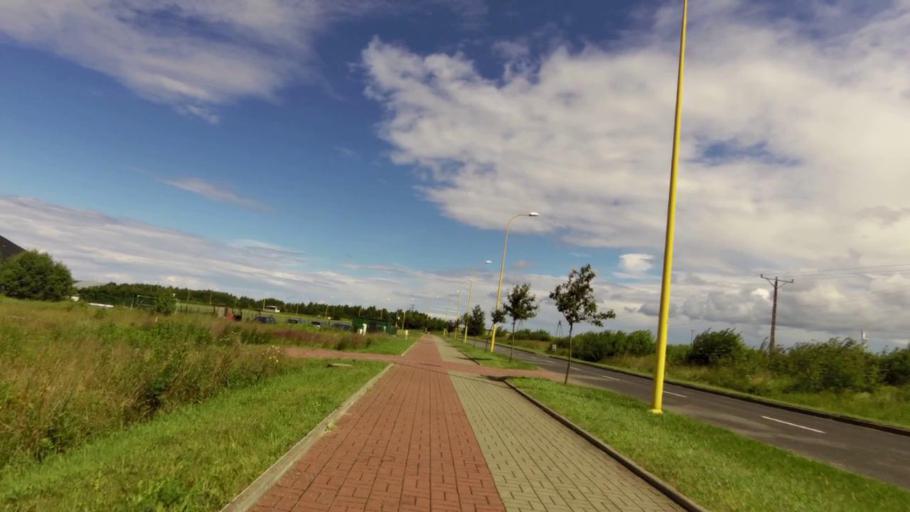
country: PL
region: West Pomeranian Voivodeship
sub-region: Powiat slawienski
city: Darlowo
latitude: 54.4406
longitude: 16.4070
